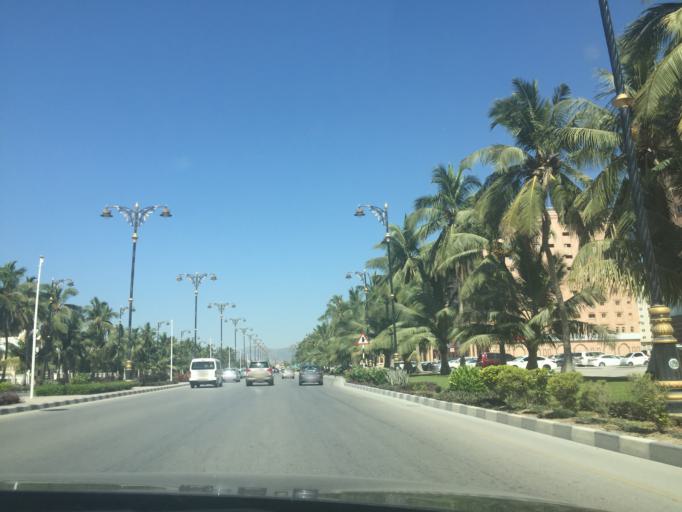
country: OM
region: Zufar
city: Salalah
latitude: 17.0194
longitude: 54.0922
